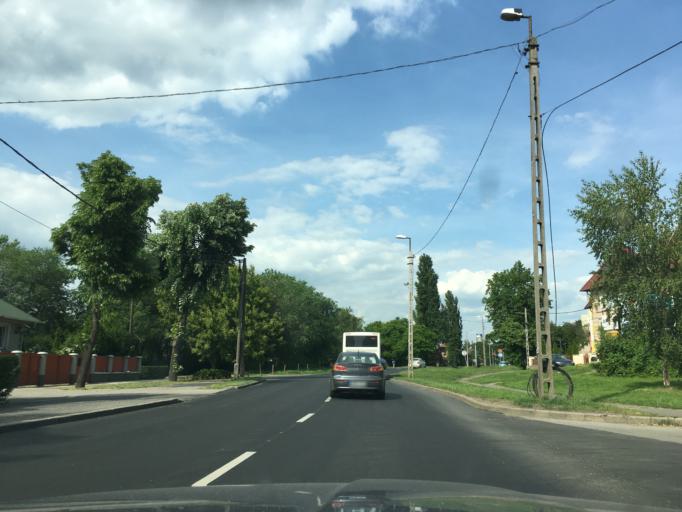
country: HU
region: Hajdu-Bihar
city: Debrecen
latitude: 47.5184
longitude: 21.6111
